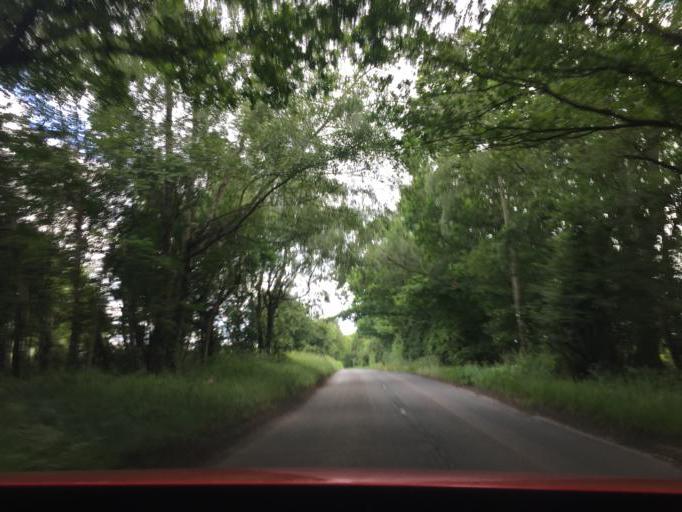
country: GB
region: England
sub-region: Hertfordshire
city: Harpenden
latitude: 51.8572
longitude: -0.3578
